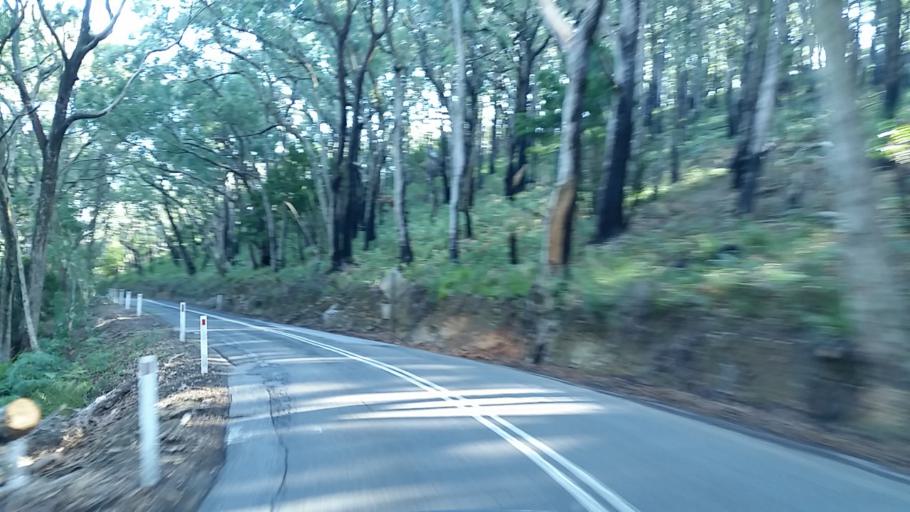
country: AU
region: South Australia
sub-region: Adelaide Hills
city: Crafers
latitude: -34.9688
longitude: 138.7137
